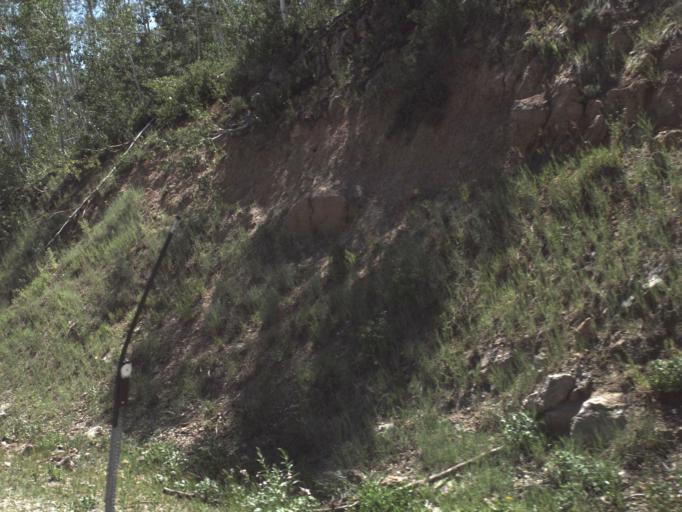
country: US
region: Utah
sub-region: Rich County
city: Randolph
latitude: 41.4751
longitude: -111.4712
